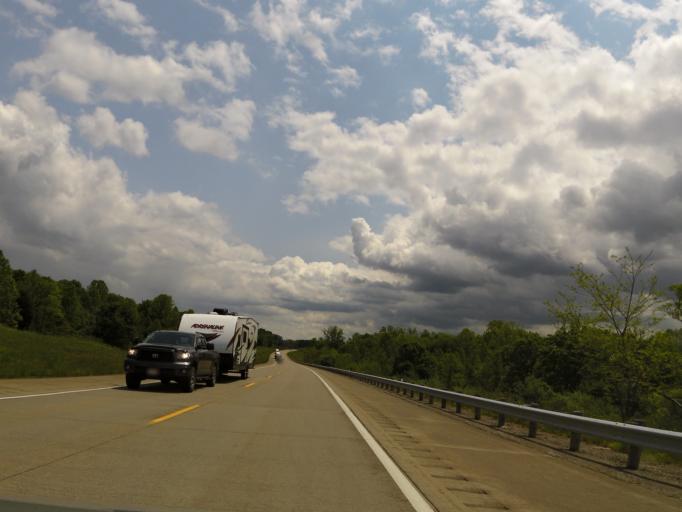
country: US
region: West Virginia
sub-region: Mason County
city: New Haven
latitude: 39.0104
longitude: -81.9084
